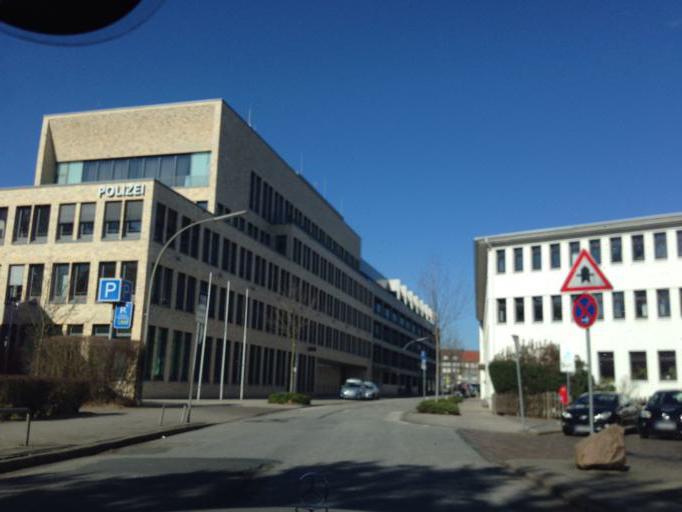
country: DE
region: Hamburg
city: Marienthal
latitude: 53.5705
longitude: 10.0715
